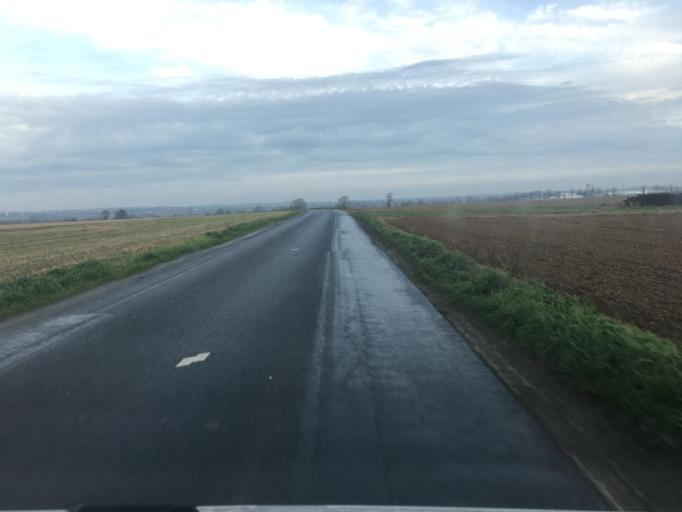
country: FR
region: Lower Normandy
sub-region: Departement du Calvados
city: Creully
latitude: 49.2632
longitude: -0.5595
